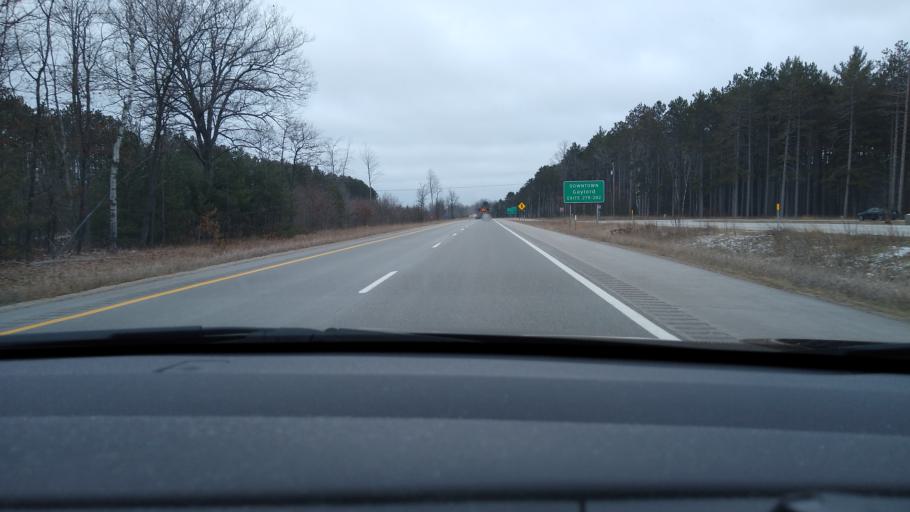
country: US
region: Michigan
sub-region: Otsego County
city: Gaylord
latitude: 44.9677
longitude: -84.6717
